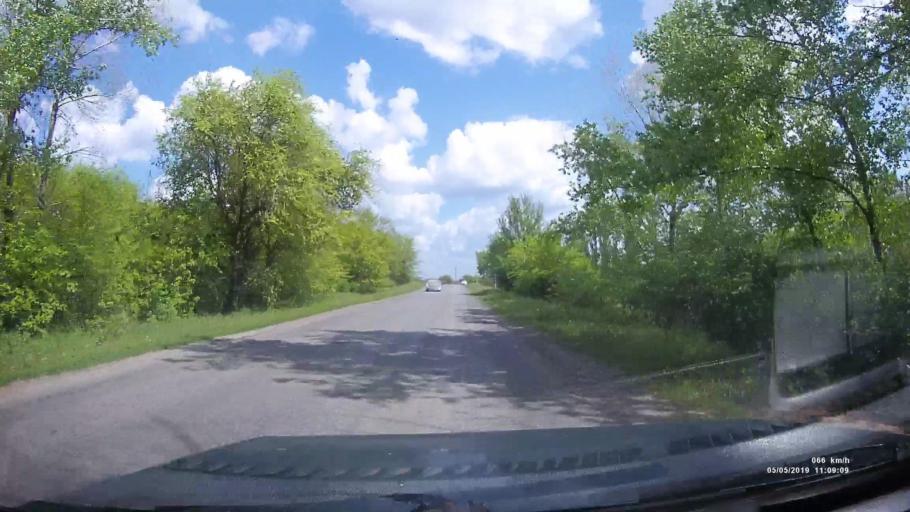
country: RU
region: Rostov
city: Ust'-Donetskiy
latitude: 47.7391
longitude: 40.9215
